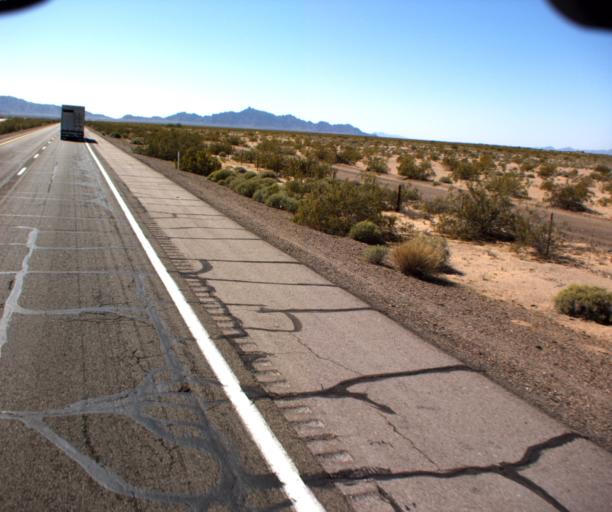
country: US
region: Arizona
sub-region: Yuma County
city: Wellton
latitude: 32.7704
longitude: -113.6106
